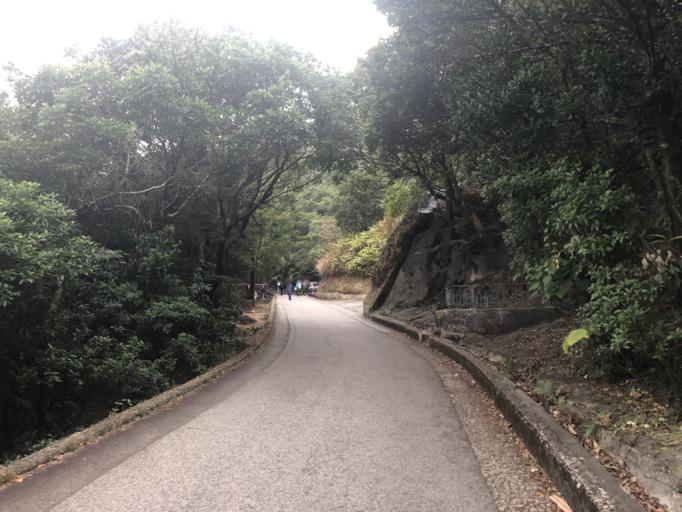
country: HK
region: Wanchai
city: Wan Chai
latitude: 22.2767
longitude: 114.2085
